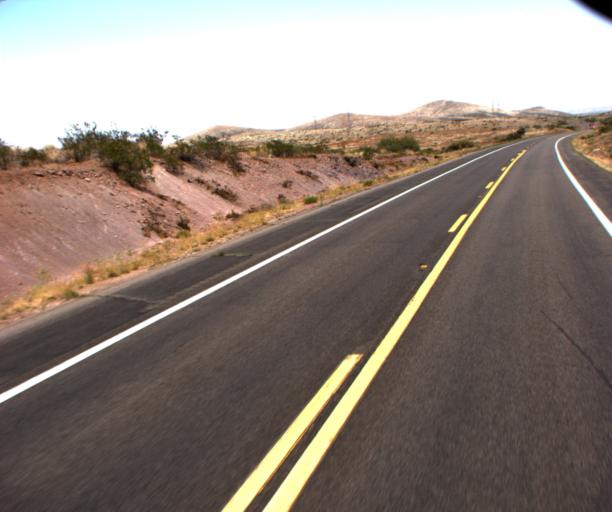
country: US
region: Arizona
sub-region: Greenlee County
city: Clifton
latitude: 32.7495
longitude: -109.2317
